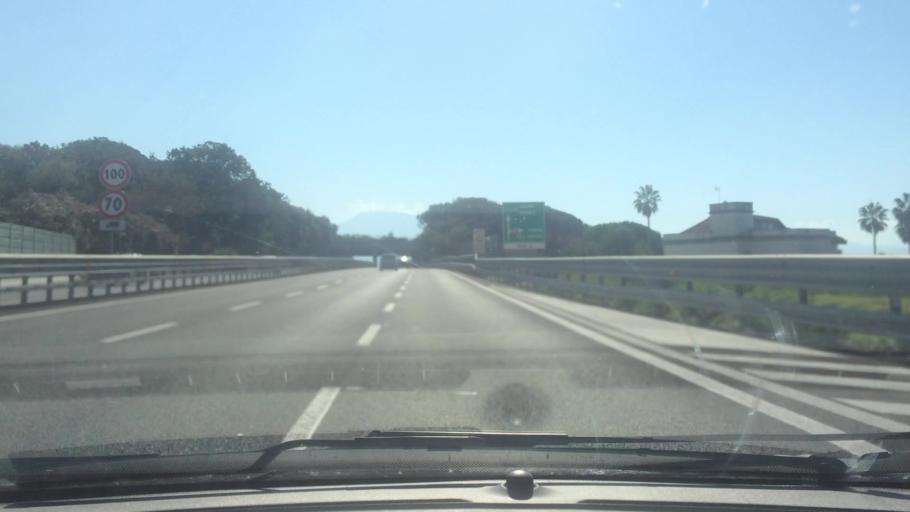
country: IT
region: Campania
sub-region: Provincia di Napoli
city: Ercolano
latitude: 40.7990
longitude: 14.3712
